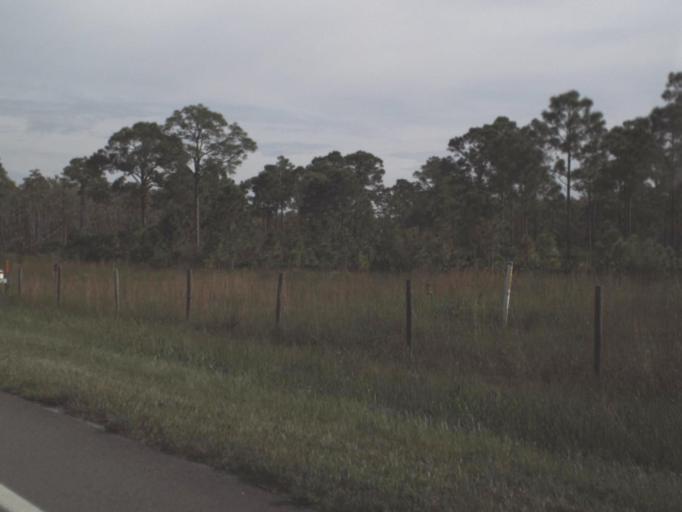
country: US
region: Florida
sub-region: Lee County
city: Olga
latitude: 26.9212
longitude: -81.7605
